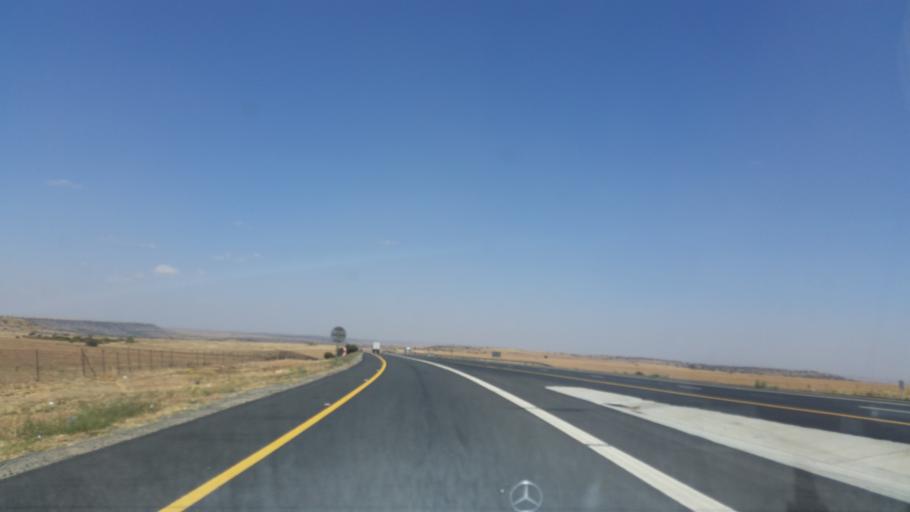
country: ZA
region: Orange Free State
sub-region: Lejweleputswa District Municipality
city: Winburg
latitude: -28.5025
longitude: 26.9962
